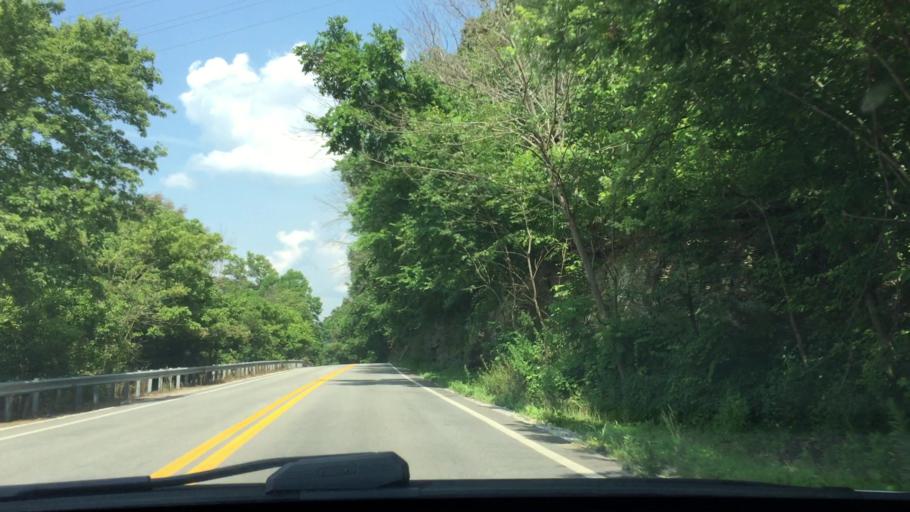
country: US
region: Ohio
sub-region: Belmont County
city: Powhatan Point
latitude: 39.7786
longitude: -80.8507
